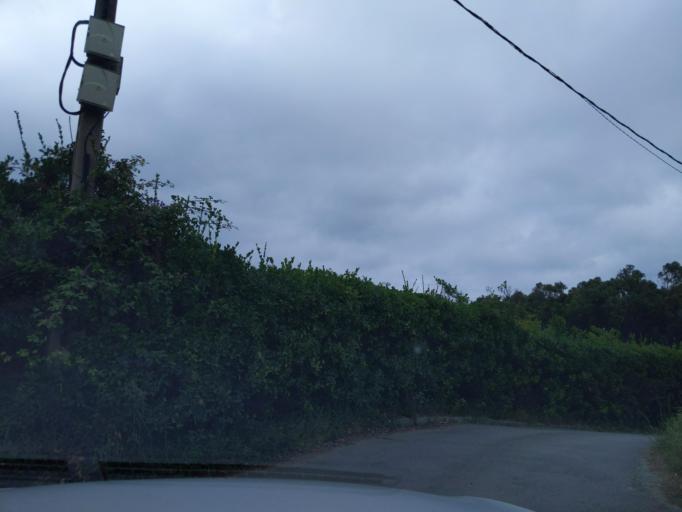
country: ES
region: Asturias
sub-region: Province of Asturias
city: Aviles
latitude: 43.6011
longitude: -5.9163
